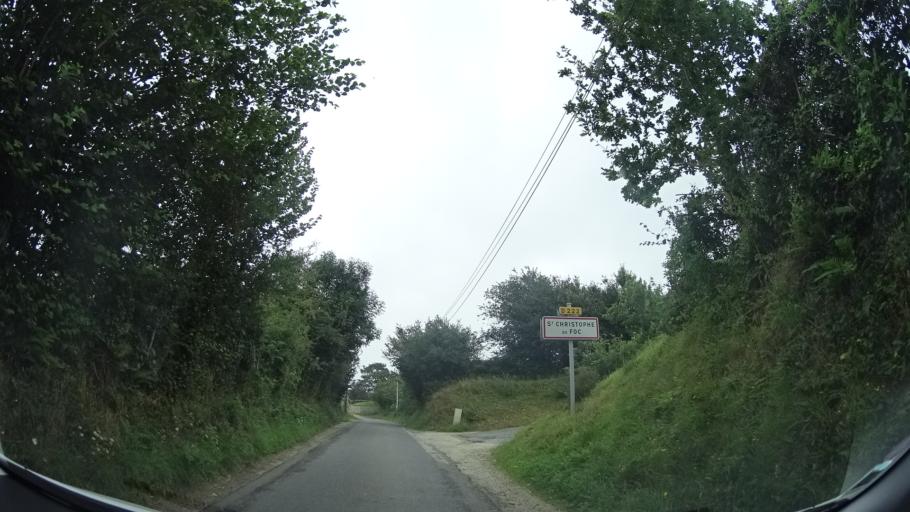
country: FR
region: Lower Normandy
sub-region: Departement de la Manche
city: Les Pieux
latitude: 49.5555
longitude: -1.7449
